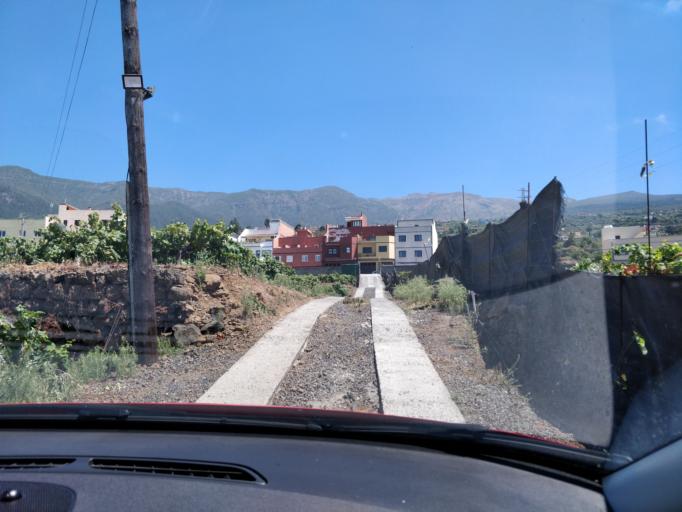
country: ES
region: Canary Islands
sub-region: Provincia de Santa Cruz de Tenerife
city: La Orotava
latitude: 28.3858
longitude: -16.5191
